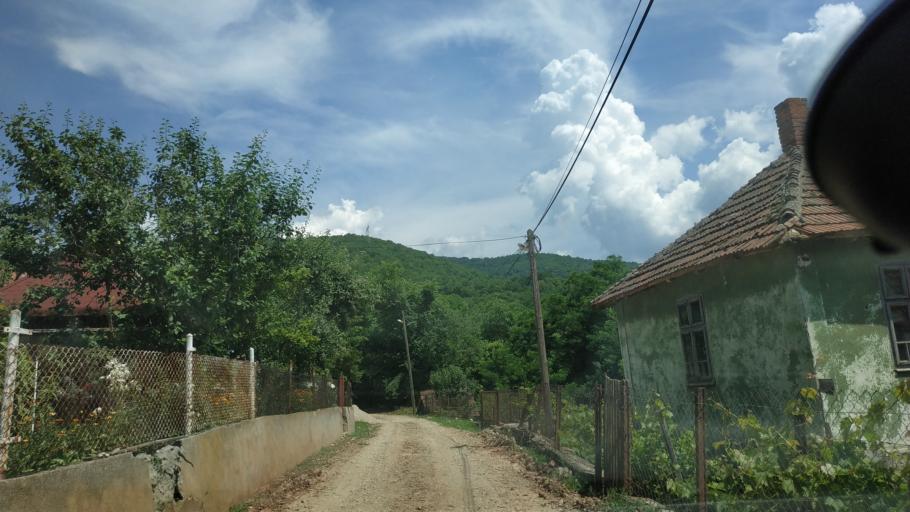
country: RS
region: Central Serbia
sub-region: Nisavski Okrug
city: Aleksinac
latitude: 43.5986
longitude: 21.6980
